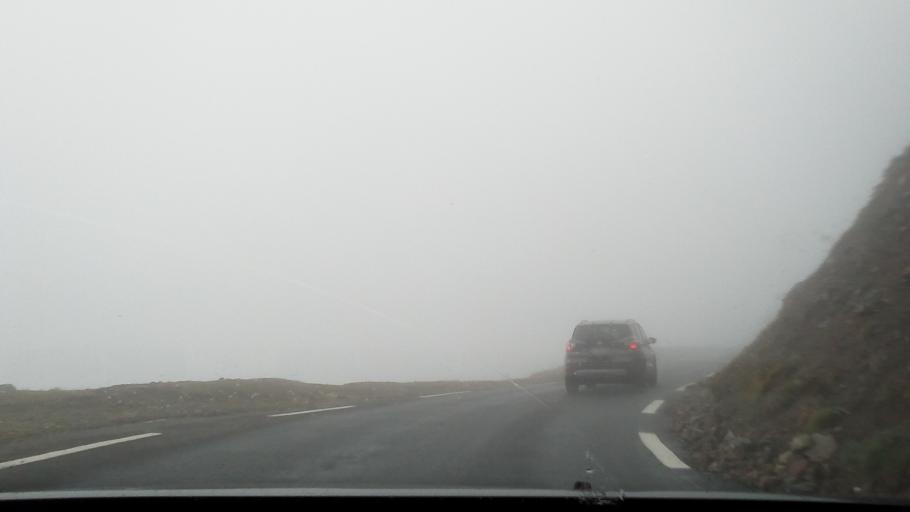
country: FR
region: Midi-Pyrenees
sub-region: Departement des Hautes-Pyrenees
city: Campan
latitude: 42.9037
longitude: 0.1287
